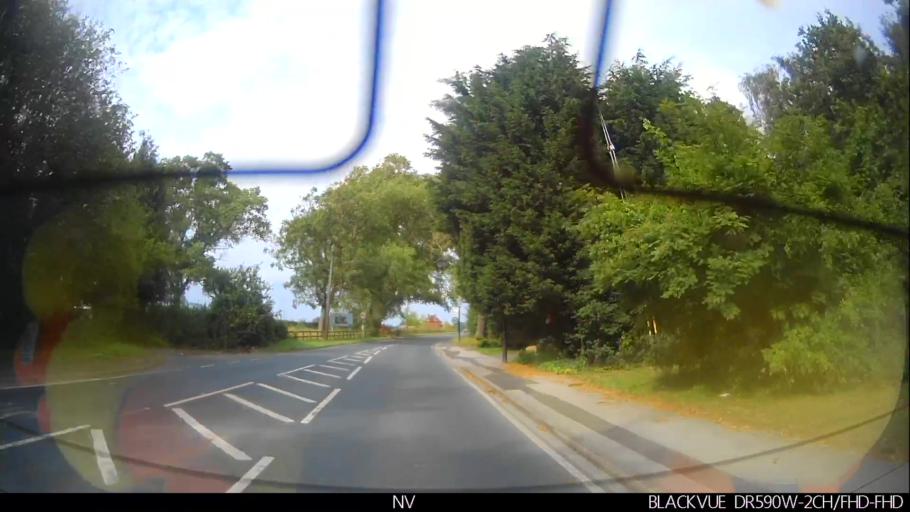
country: GB
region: England
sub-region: City of York
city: Huntington
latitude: 54.0117
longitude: -1.0527
